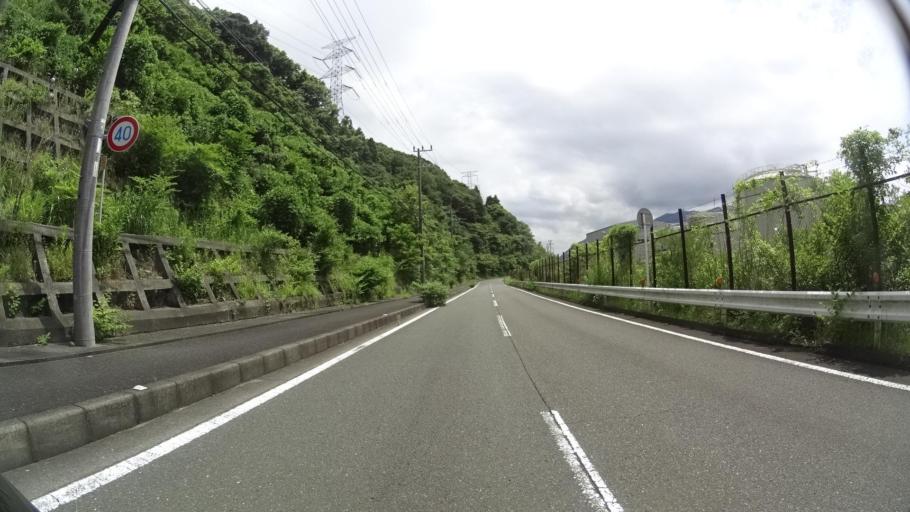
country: JP
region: Kyoto
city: Maizuru
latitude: 35.5318
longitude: 135.3471
